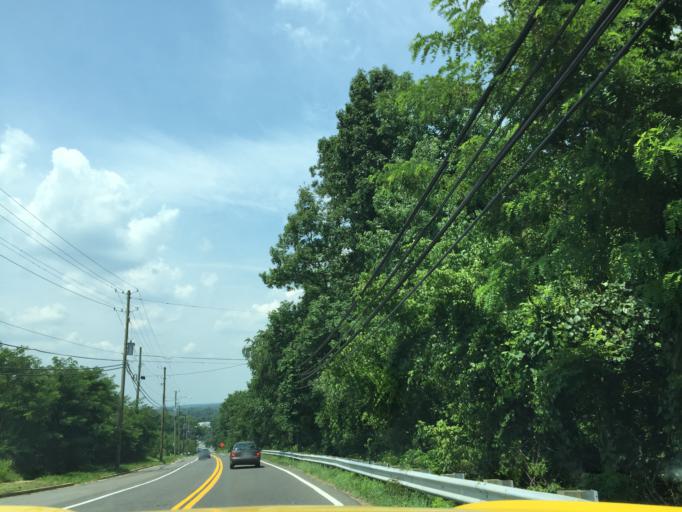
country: US
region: Maryland
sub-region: Prince George's County
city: Friendly
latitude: 38.7218
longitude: -76.9863
